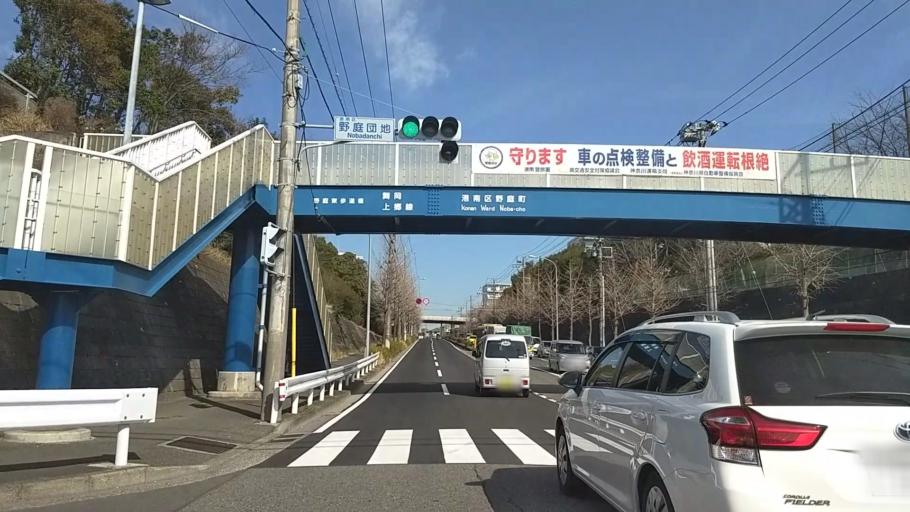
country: JP
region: Kanagawa
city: Kamakura
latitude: 35.3866
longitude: 139.5747
